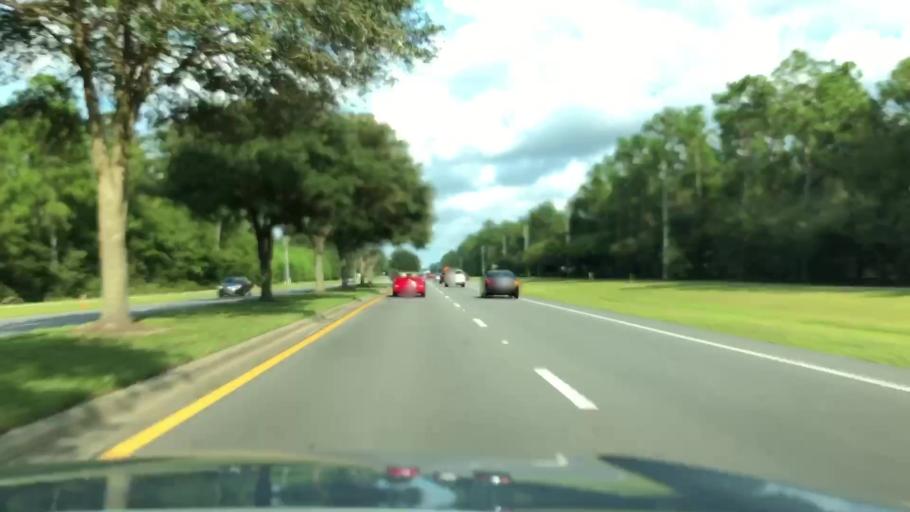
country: US
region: Florida
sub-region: Saint Johns County
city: Fruit Cove
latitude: 30.1103
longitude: -81.5703
